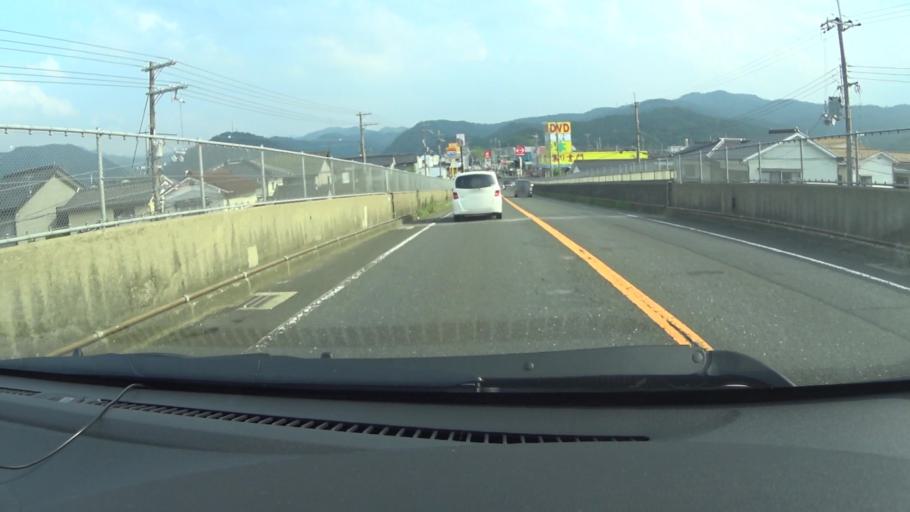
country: JP
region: Kyoto
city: Maizuru
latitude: 35.4332
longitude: 135.3283
